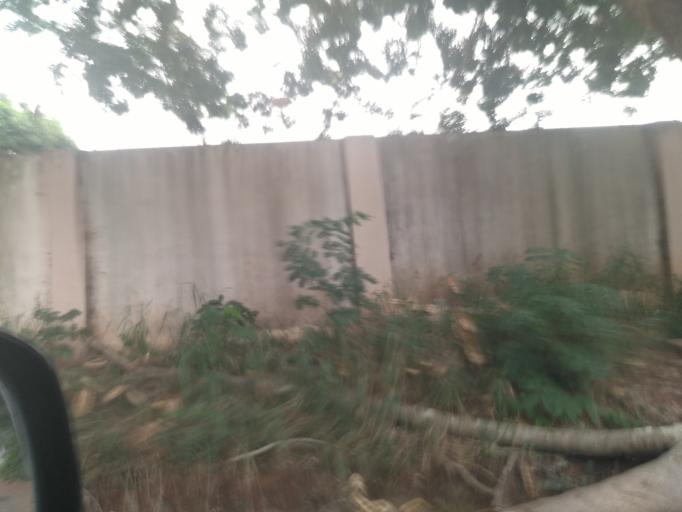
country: GH
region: Greater Accra
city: Accra
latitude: 5.6060
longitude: -0.1862
